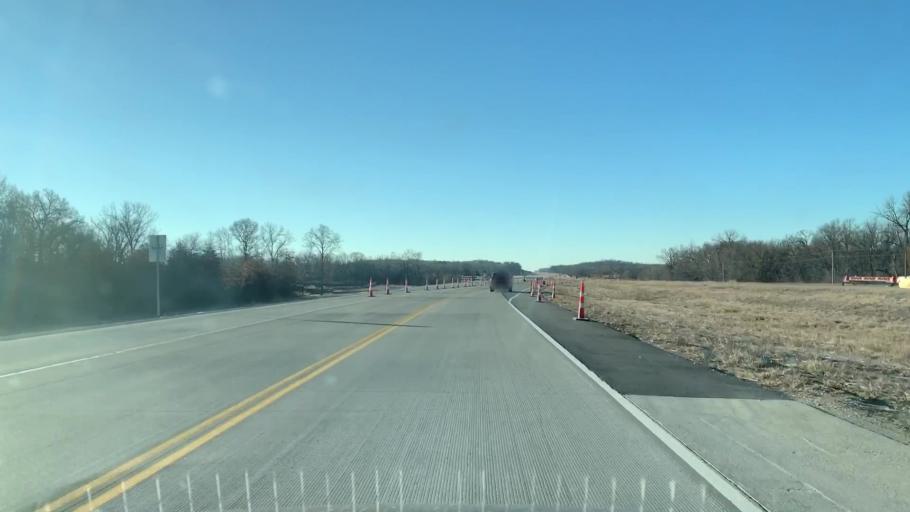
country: US
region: Kansas
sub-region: Crawford County
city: Arma
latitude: 37.6788
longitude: -94.7031
